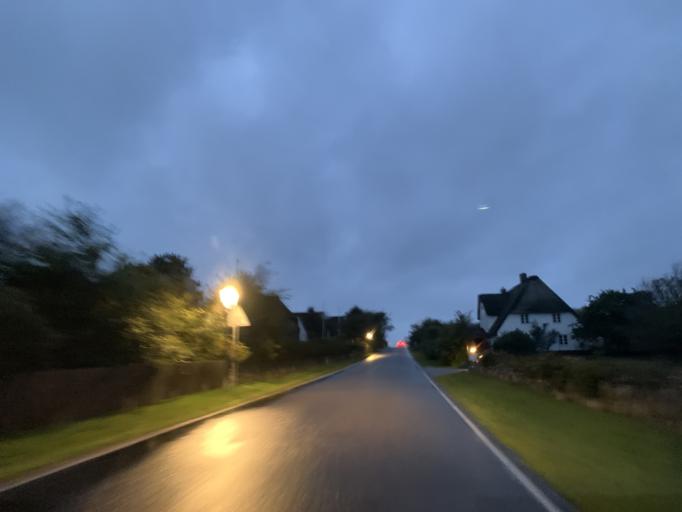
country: DE
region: Schleswig-Holstein
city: Wittdun
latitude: 54.6380
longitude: 8.3772
